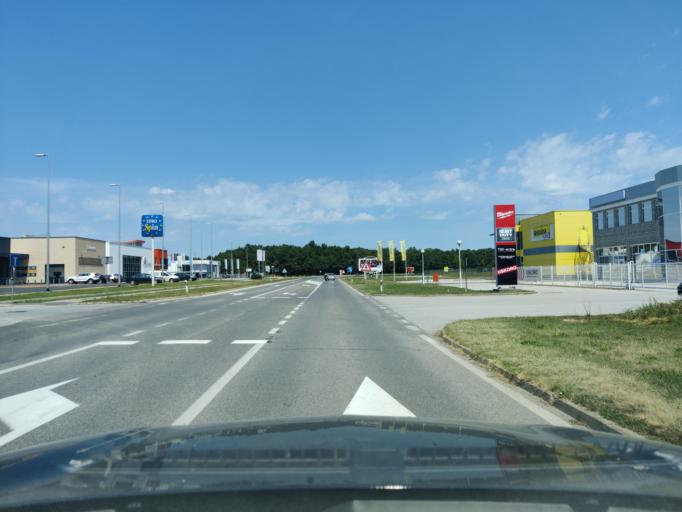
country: HR
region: Medimurska
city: Cakovec
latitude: 46.3889
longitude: 16.4150
